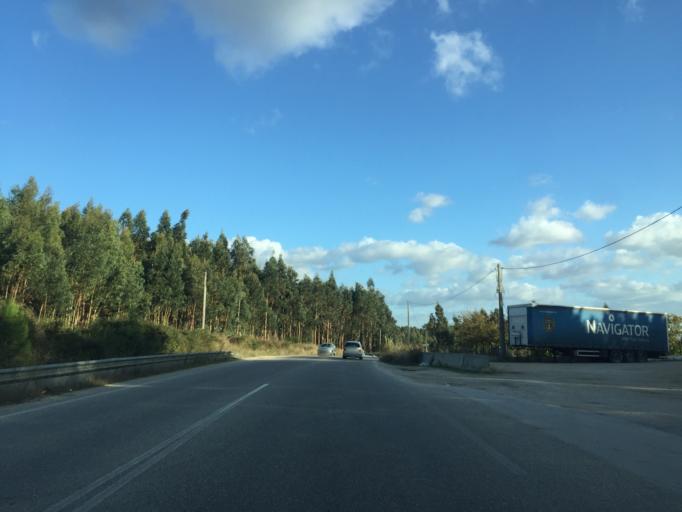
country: PT
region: Leiria
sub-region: Leiria
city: Amor
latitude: 39.8090
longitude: -8.8416
